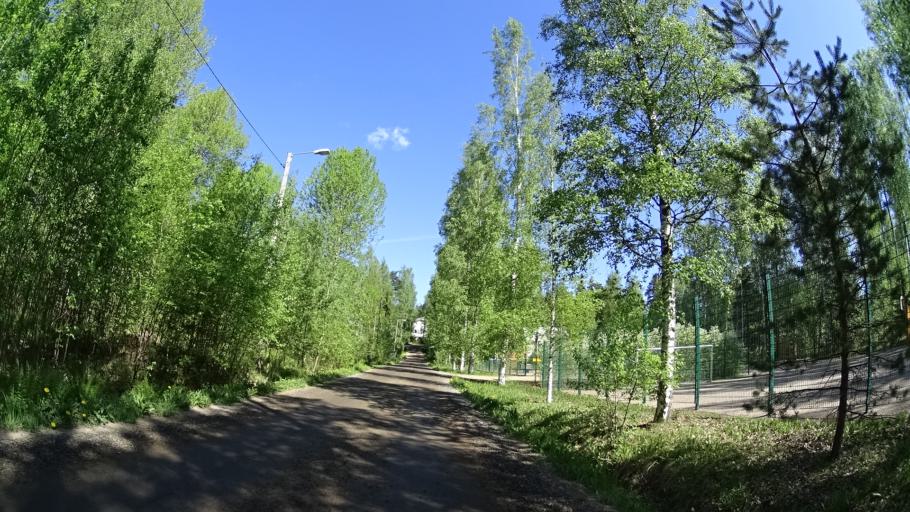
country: FI
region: Uusimaa
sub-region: Helsinki
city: Espoo
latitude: 60.1597
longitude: 24.6179
